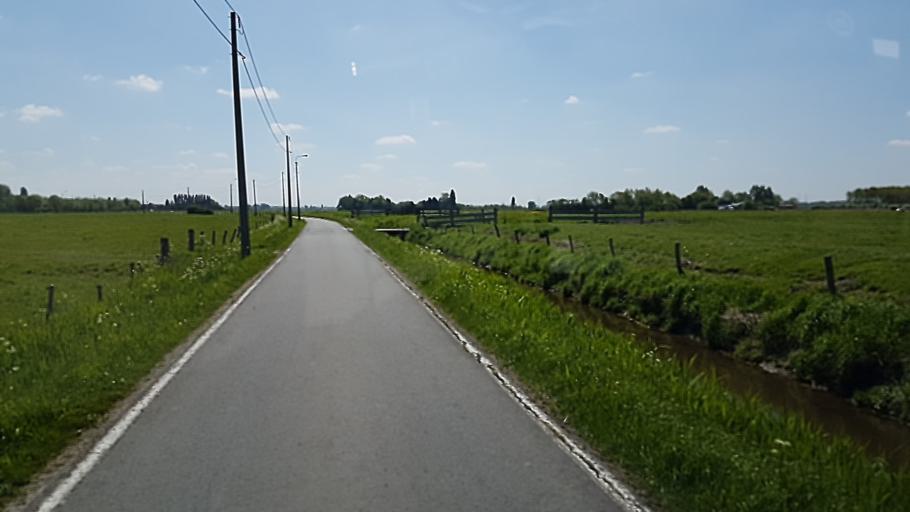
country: BE
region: Flanders
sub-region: Provincie West-Vlaanderen
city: De Haan
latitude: 51.2426
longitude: 3.0473
